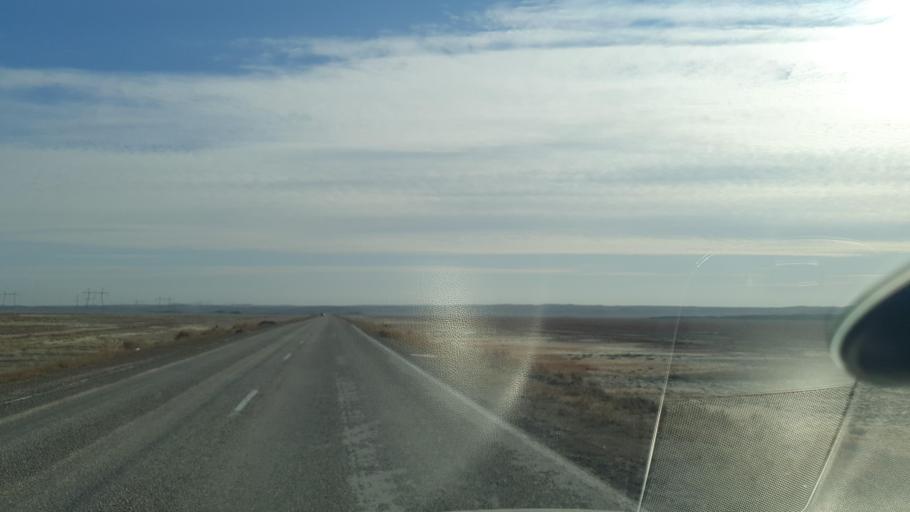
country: KZ
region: Zhambyl
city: Mynaral
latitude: 45.5807
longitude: 73.4099
